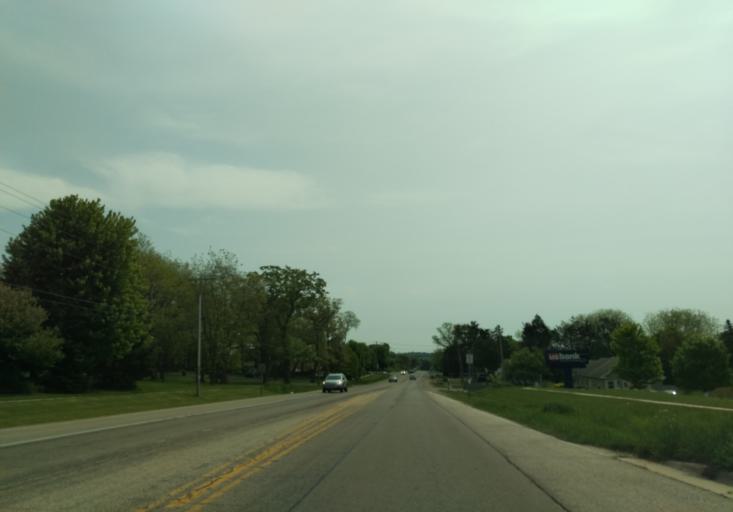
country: US
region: Wisconsin
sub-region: Dane County
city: Monona
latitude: 43.0848
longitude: -89.2702
